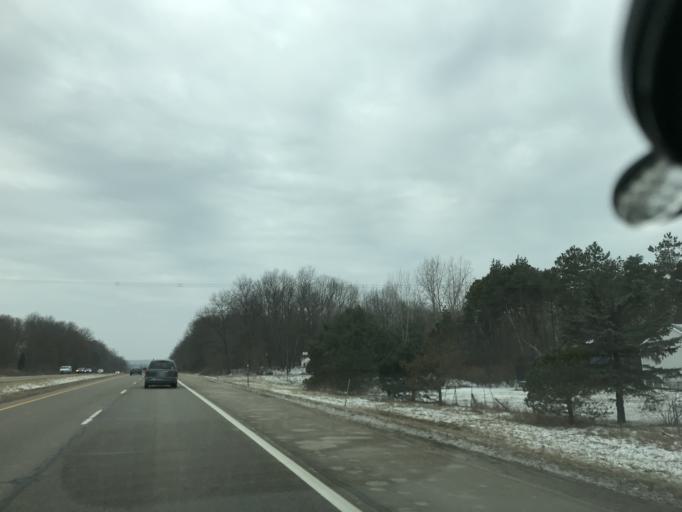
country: US
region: Michigan
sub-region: Kent County
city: Rockford
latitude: 43.0830
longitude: -85.5584
